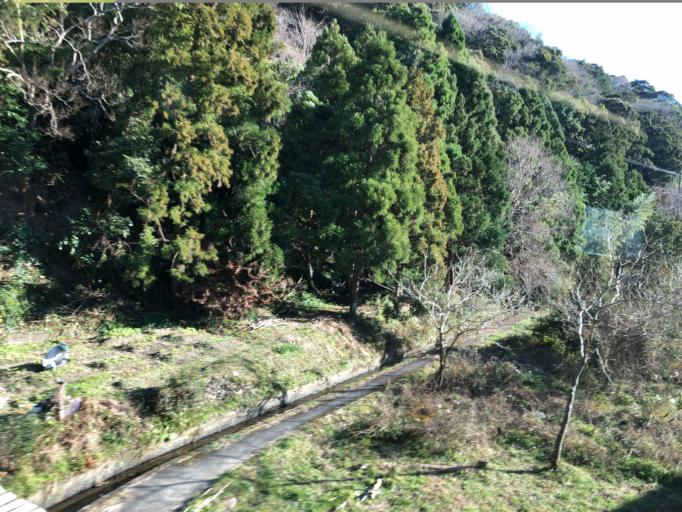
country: JP
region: Kochi
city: Nakamura
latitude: 33.0863
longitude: 133.1029
